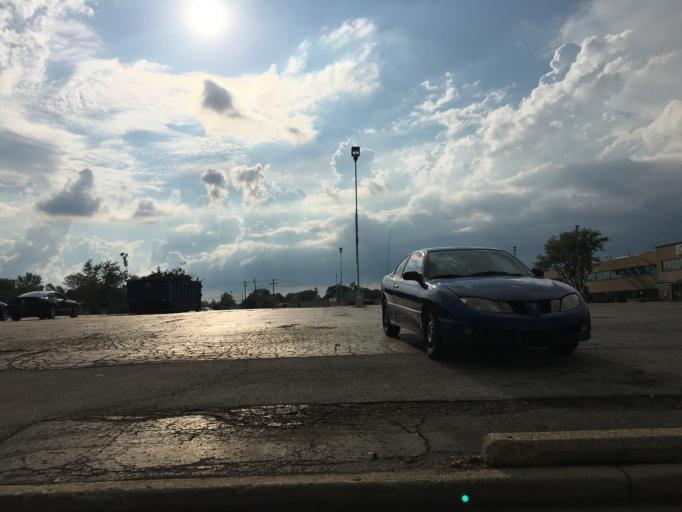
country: US
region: Indiana
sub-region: Howard County
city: Kokomo
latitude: 40.4676
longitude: -86.1221
